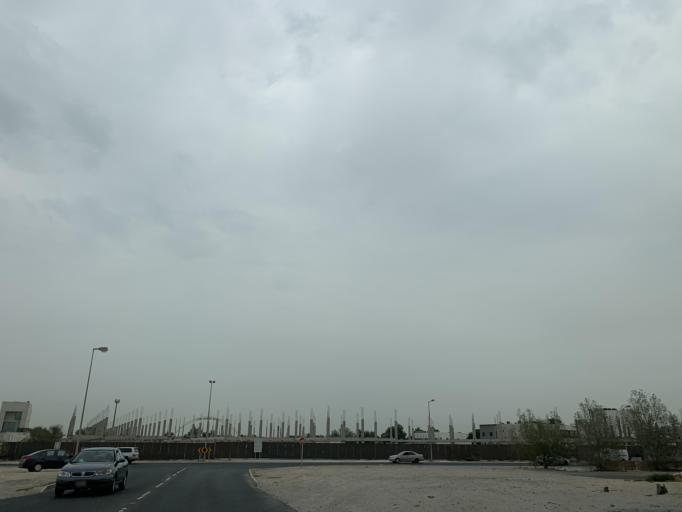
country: BH
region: Manama
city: Jidd Hafs
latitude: 26.1961
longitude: 50.4757
